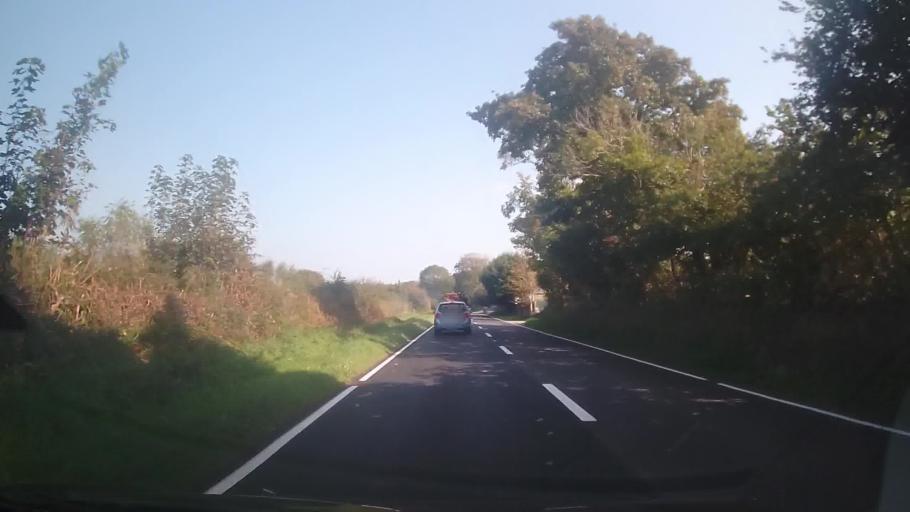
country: GB
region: Wales
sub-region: Pembrokeshire
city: Newport
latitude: 52.0159
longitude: -4.8188
